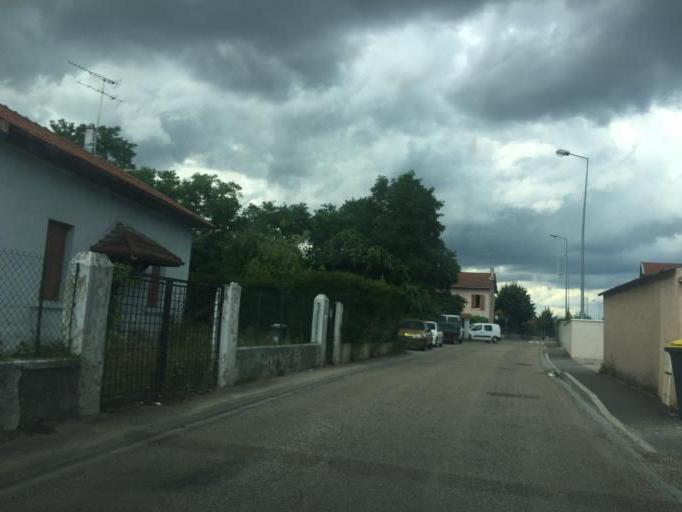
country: FR
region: Rhone-Alpes
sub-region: Departement de l'Isere
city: Charvieu-Chavagneux
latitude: 45.7528
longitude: 5.1673
